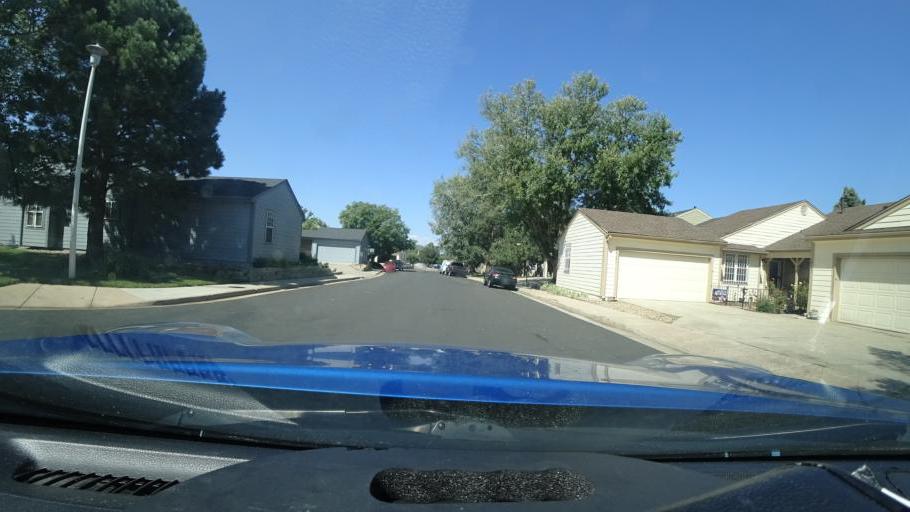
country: US
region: Colorado
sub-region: Adams County
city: Aurora
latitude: 39.6762
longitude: -104.8227
